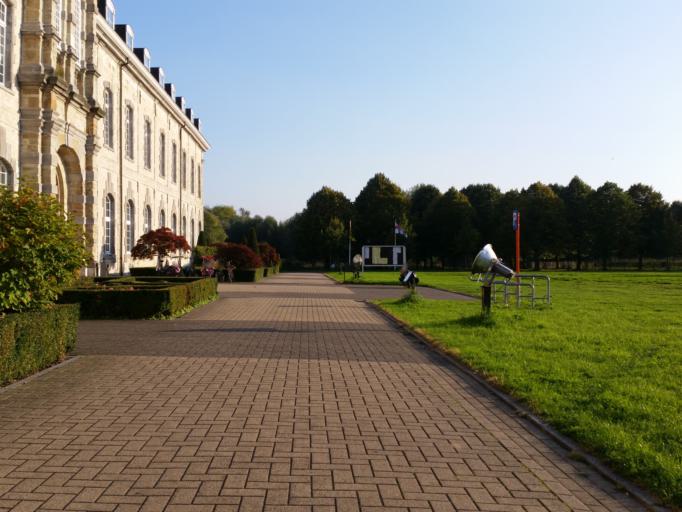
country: BE
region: Flanders
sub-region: Provincie Antwerpen
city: Schelle
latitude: 51.1316
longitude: 4.3291
